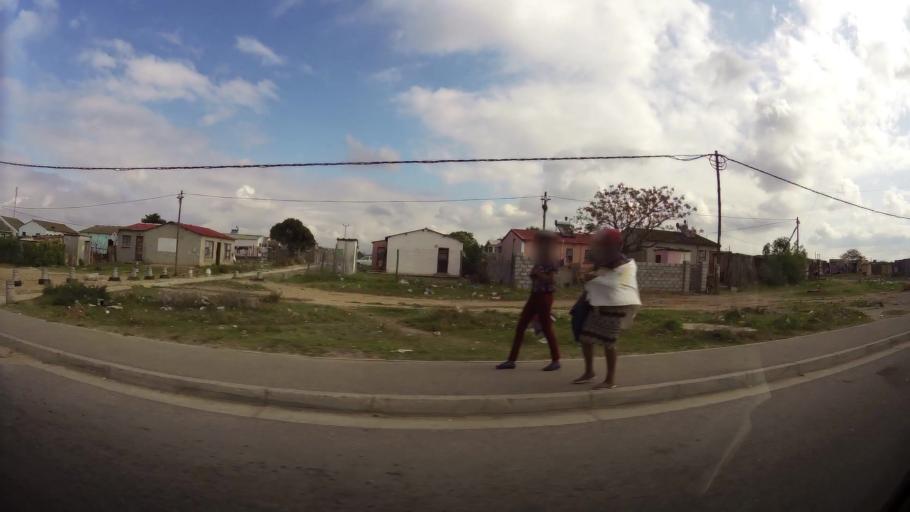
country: ZA
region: Eastern Cape
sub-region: Nelson Mandela Bay Metropolitan Municipality
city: Port Elizabeth
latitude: -33.8001
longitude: 25.5852
